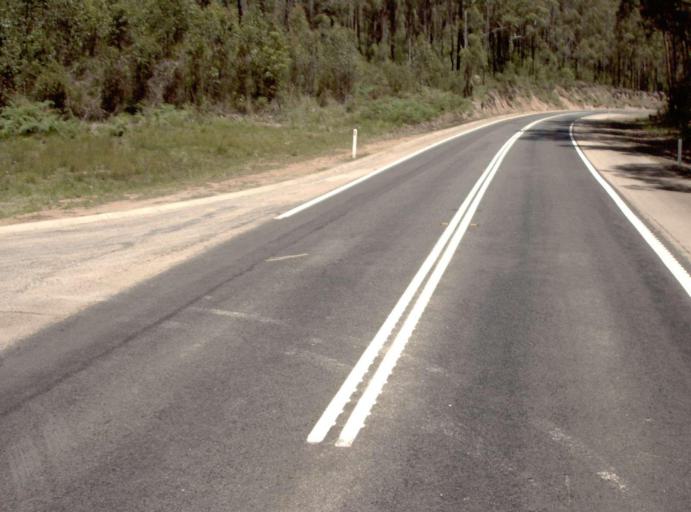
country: AU
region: New South Wales
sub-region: Bombala
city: Bombala
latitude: -37.6050
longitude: 148.9045
